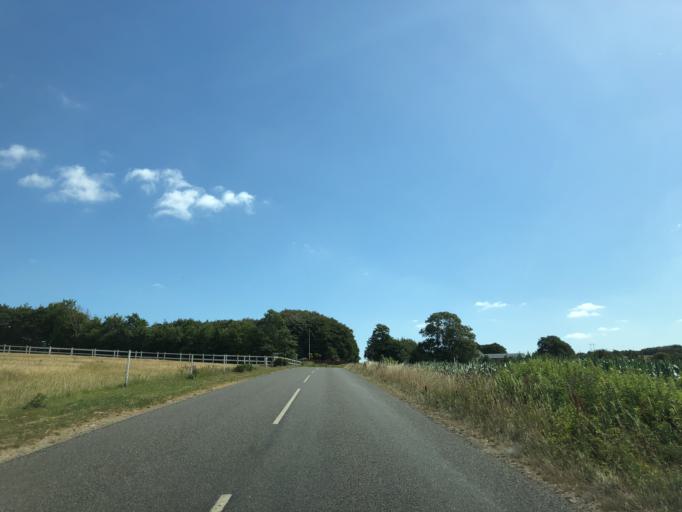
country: DK
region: North Denmark
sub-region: Vesthimmerland Kommune
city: Alestrup
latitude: 56.5759
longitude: 9.5220
